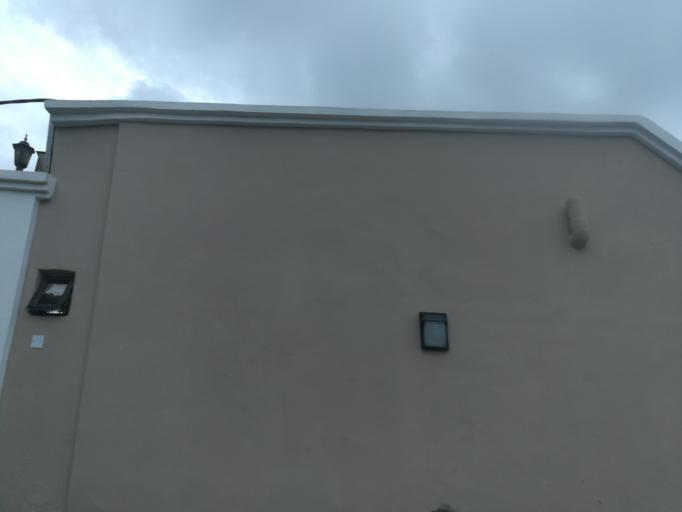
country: NG
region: Lagos
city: Ikoyi
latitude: 6.4401
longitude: 3.4185
